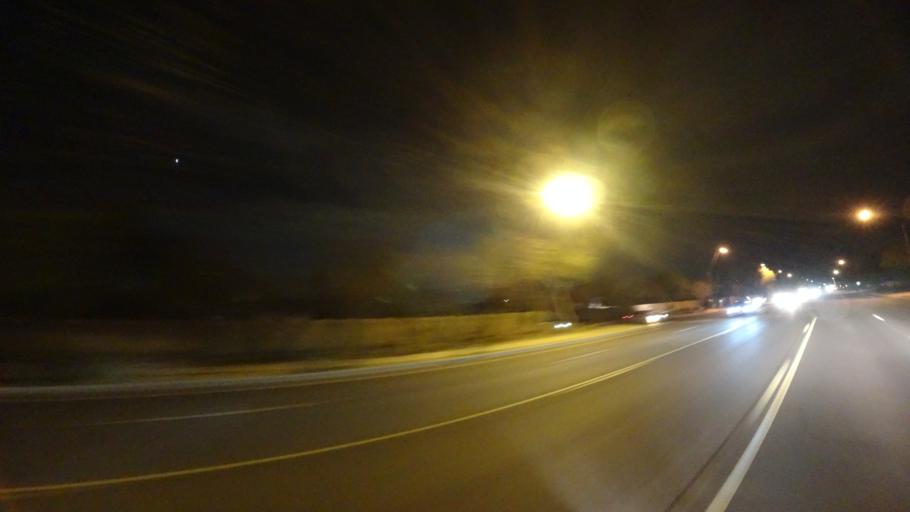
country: US
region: Arizona
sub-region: Maricopa County
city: Gilbert
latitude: 33.3248
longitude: -111.7730
